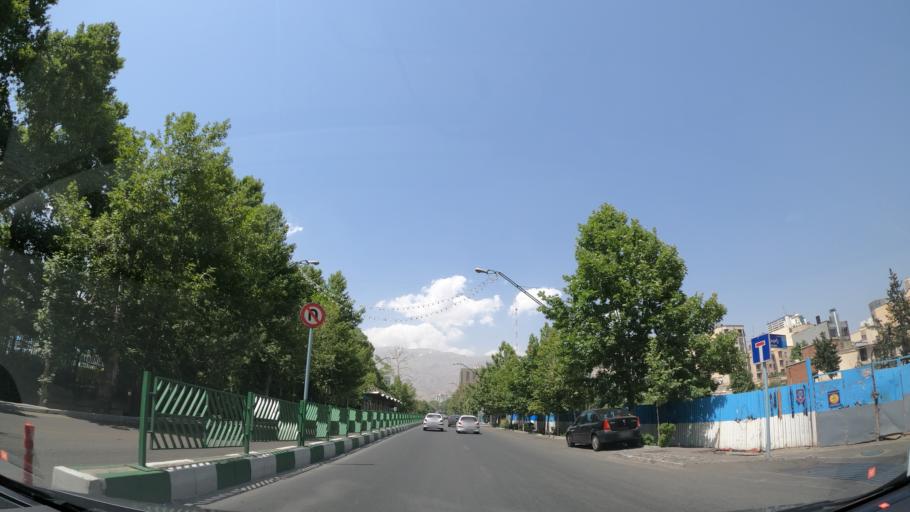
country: IR
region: Tehran
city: Tajrish
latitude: 35.7825
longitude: 51.4144
